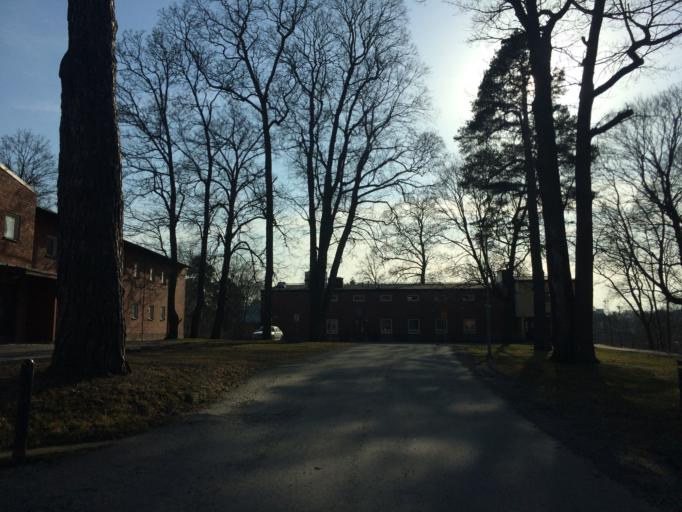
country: SE
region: Stockholm
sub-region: Stockholms Kommun
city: Stockholm
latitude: 59.3575
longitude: 18.0528
